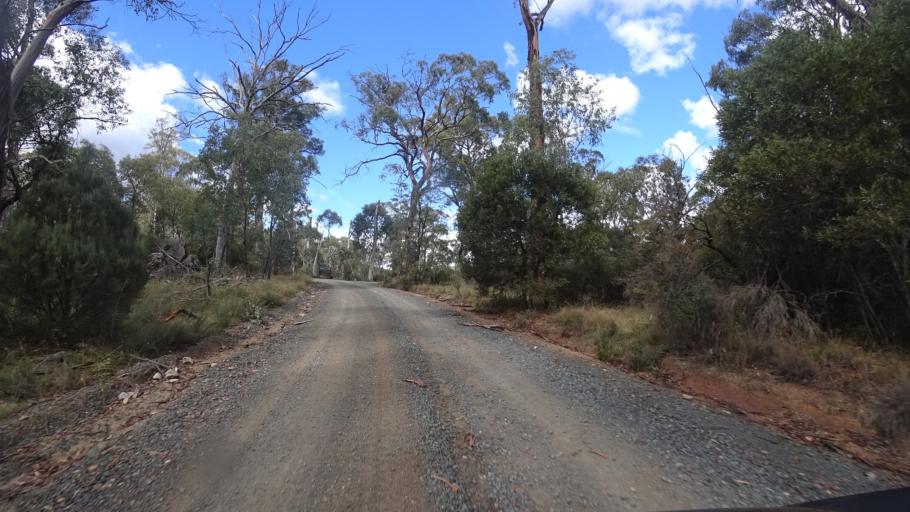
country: AU
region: New South Wales
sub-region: Tumut Shire
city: Tumut
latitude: -35.7219
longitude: 148.4897
